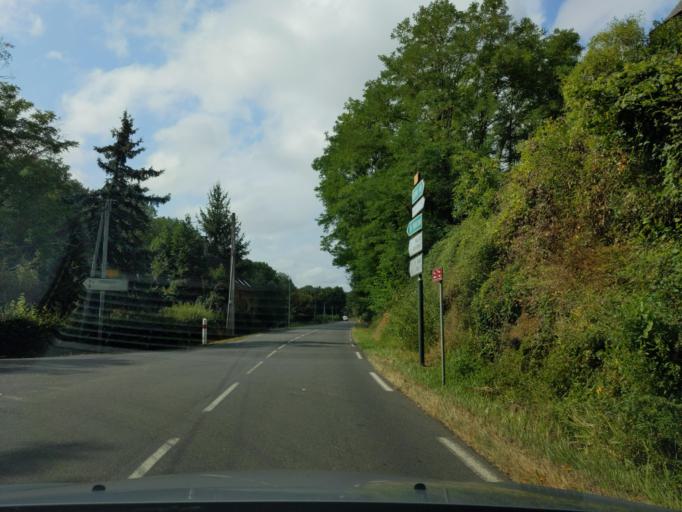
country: FR
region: Bourgogne
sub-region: Departement de Saone-et-Loire
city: Bourbon-Lancy
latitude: 46.6984
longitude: 3.8645
